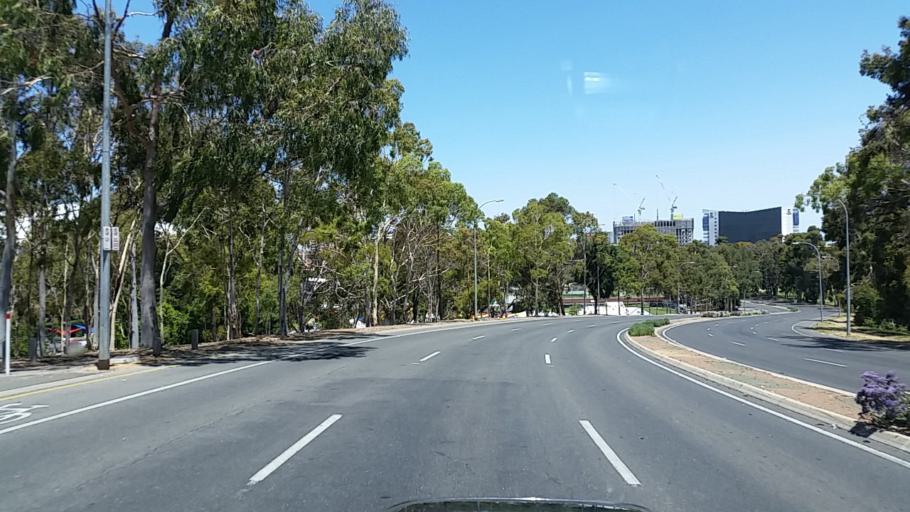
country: AU
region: South Australia
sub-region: Adelaide
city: North Adelaide
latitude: -34.9133
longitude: 138.5937
